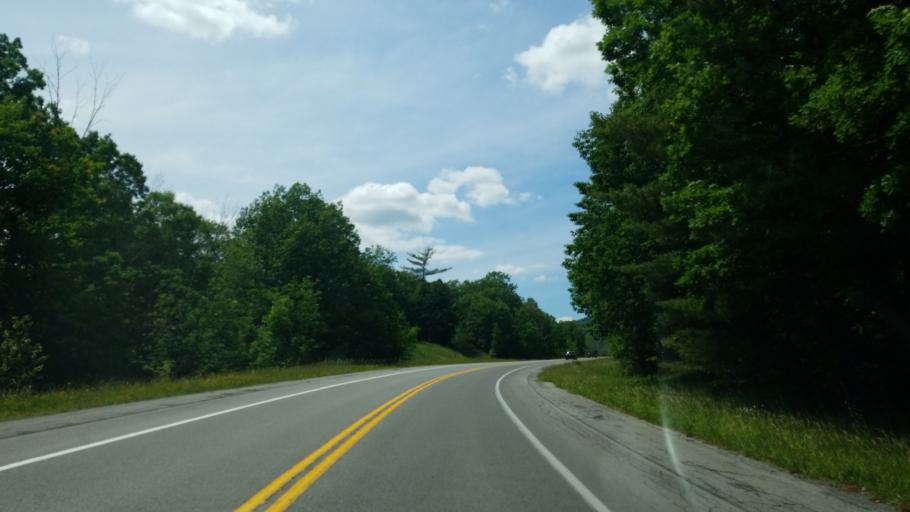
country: US
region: Pennsylvania
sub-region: Blair County
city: Tyrone
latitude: 40.6815
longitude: -78.2608
